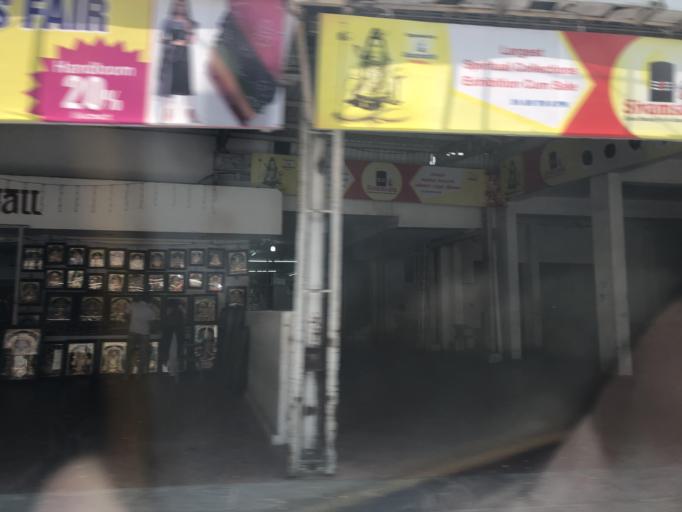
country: IN
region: Tamil Nadu
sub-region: Chennai
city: Chetput
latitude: 13.0427
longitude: 80.2593
